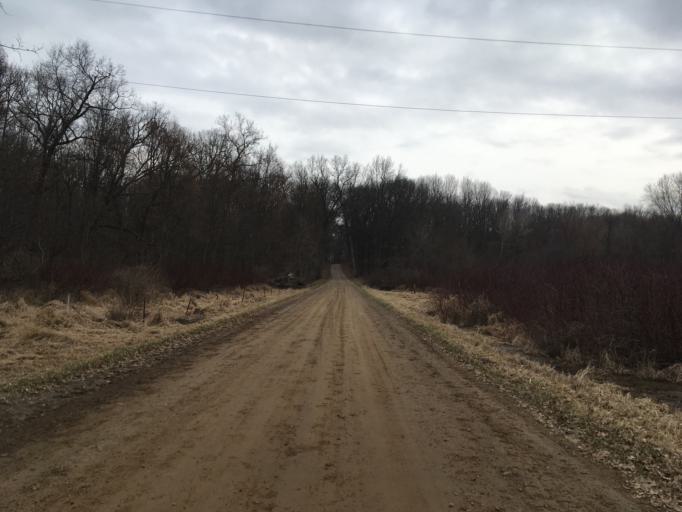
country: US
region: Michigan
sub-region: Jackson County
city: Grass Lake
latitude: 42.3240
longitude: -84.1950
